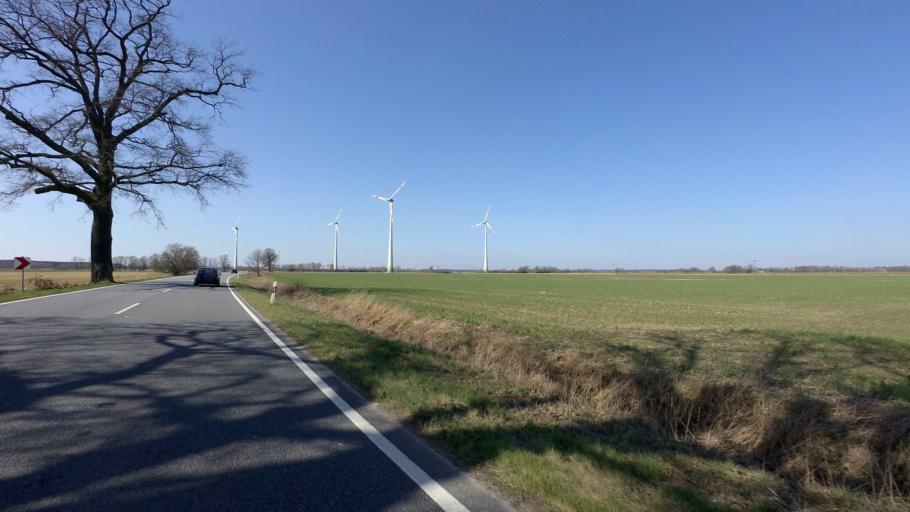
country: DE
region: Brandenburg
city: Ruthnick
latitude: 52.9010
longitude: 13.0257
